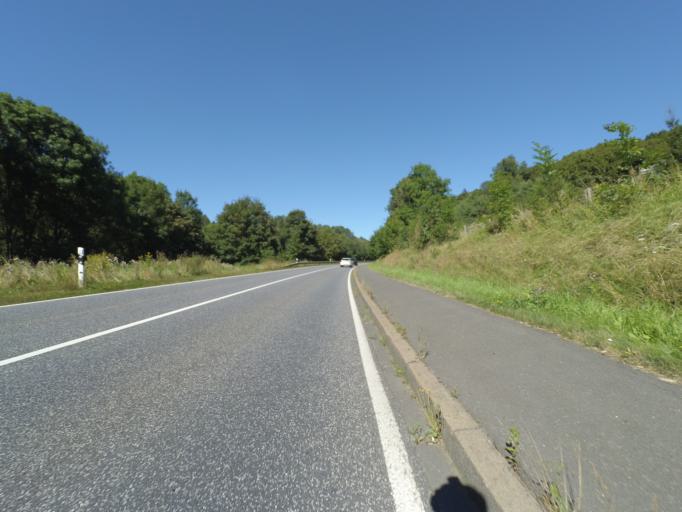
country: DE
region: Rheinland-Pfalz
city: Pelm
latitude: 50.2265
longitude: 6.6794
